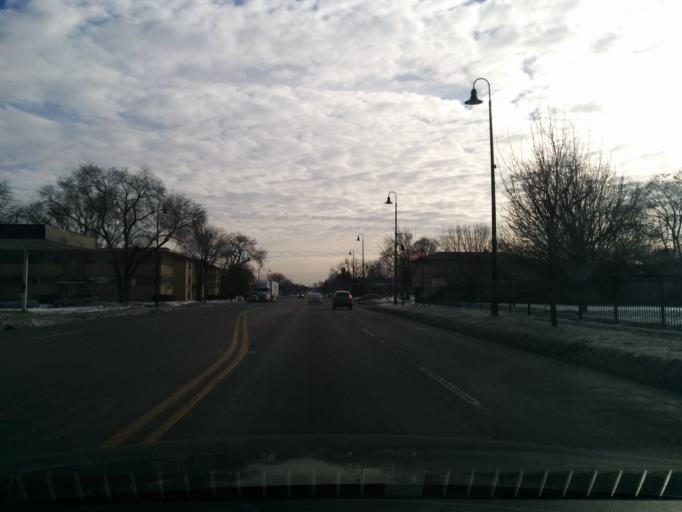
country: US
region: Illinois
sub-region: Cook County
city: Berkeley
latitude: 41.8895
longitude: -87.9126
